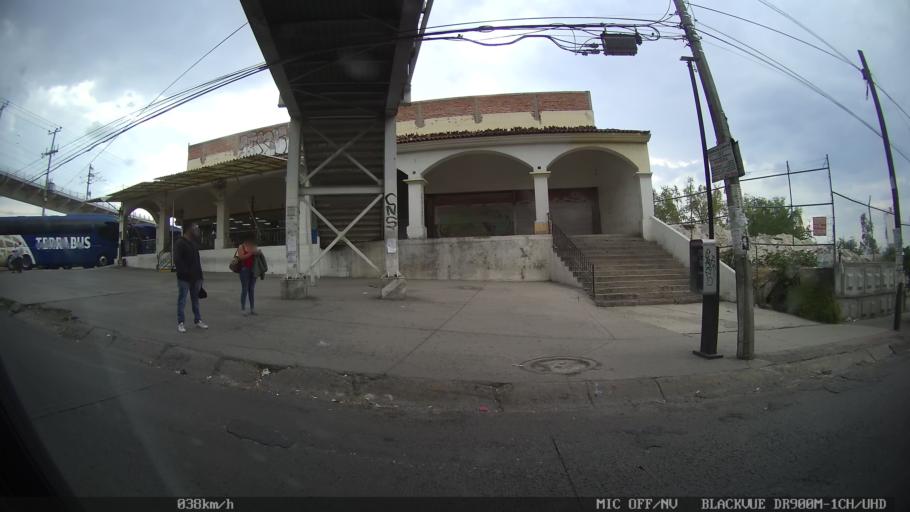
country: MX
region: Jalisco
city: Tlaquepaque
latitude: 20.6245
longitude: -103.2875
